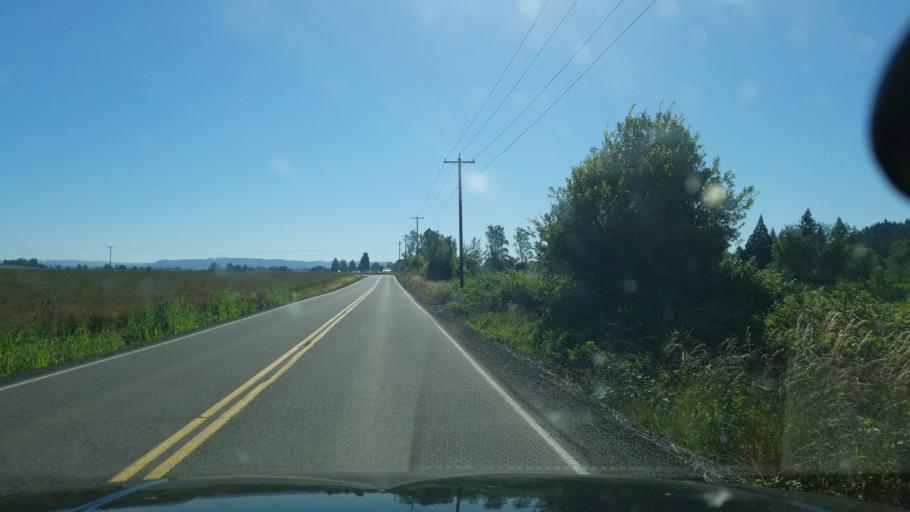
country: US
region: Oregon
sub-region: Yamhill County
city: McMinnville
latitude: 45.2259
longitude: -123.2565
